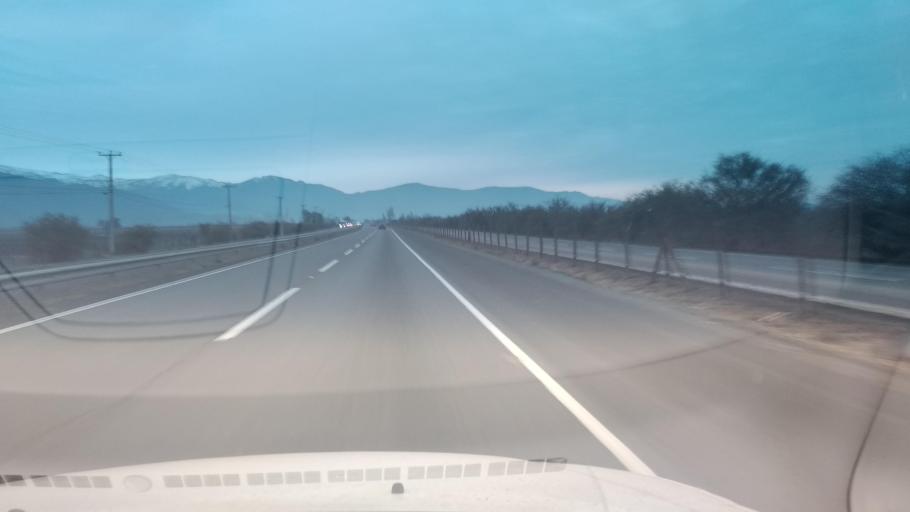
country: CL
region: Santiago Metropolitan
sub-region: Provincia de Chacabuco
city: Chicureo Abajo
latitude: -33.1505
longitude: -70.6550
